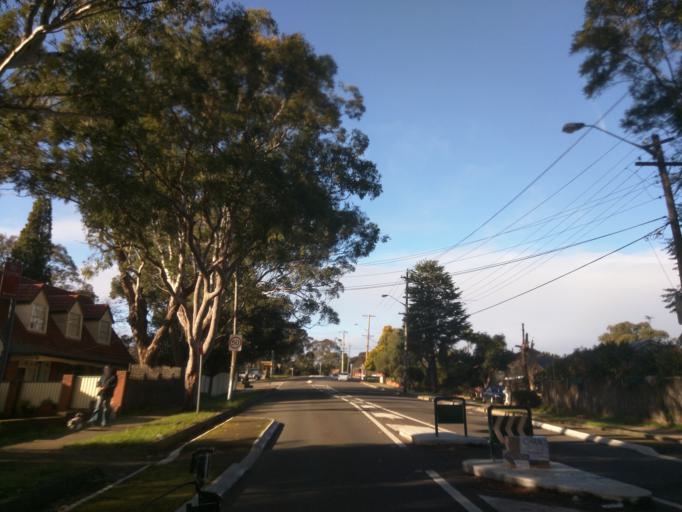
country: AU
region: New South Wales
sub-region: Hurstville
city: Lugarno
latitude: -33.9809
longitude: 151.0460
